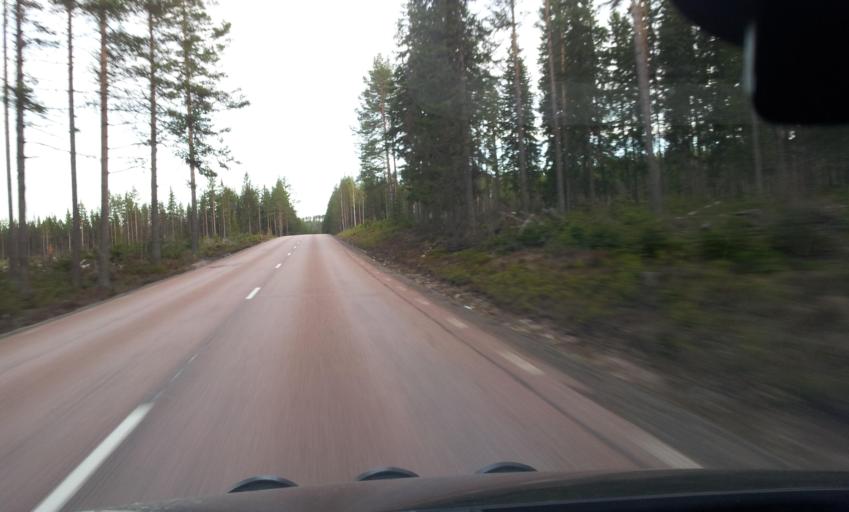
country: SE
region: Gaevleborg
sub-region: Ljusdals Kommun
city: Farila
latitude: 61.9859
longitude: 15.8556
